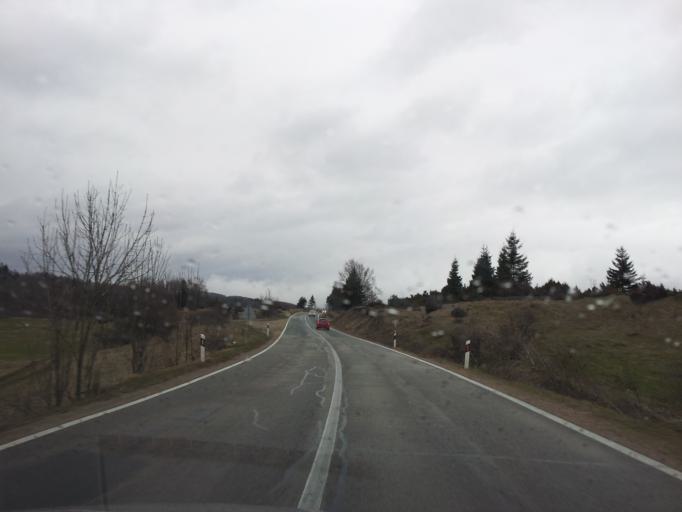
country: HR
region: Licko-Senjska
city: Jezerce
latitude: 44.8078
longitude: 15.6831
